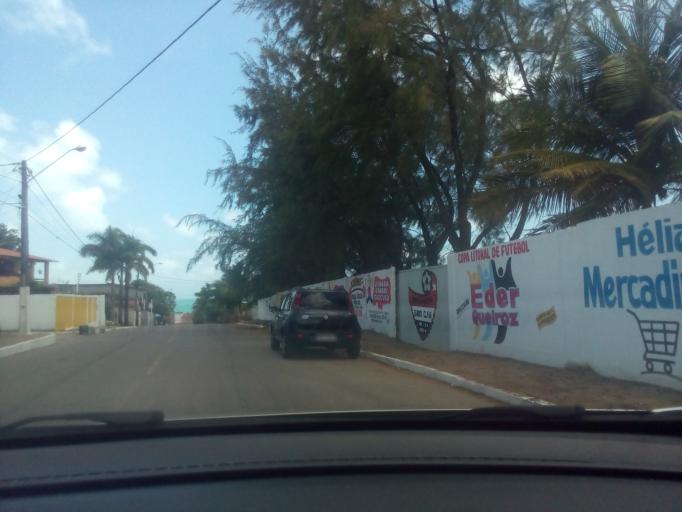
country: BR
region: Rio Grande do Norte
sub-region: Nisia Floresta
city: Nisia Floresta
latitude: -5.9719
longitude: -35.1320
